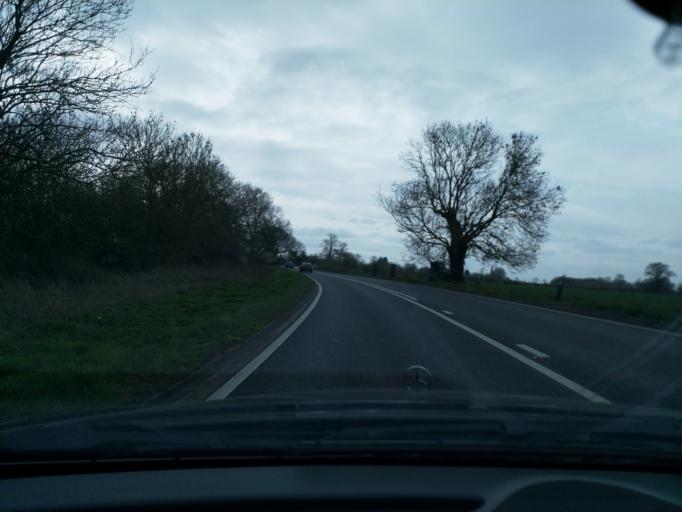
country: GB
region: England
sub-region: Warwickshire
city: Stratford-upon-Avon
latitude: 52.2372
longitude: -1.6535
